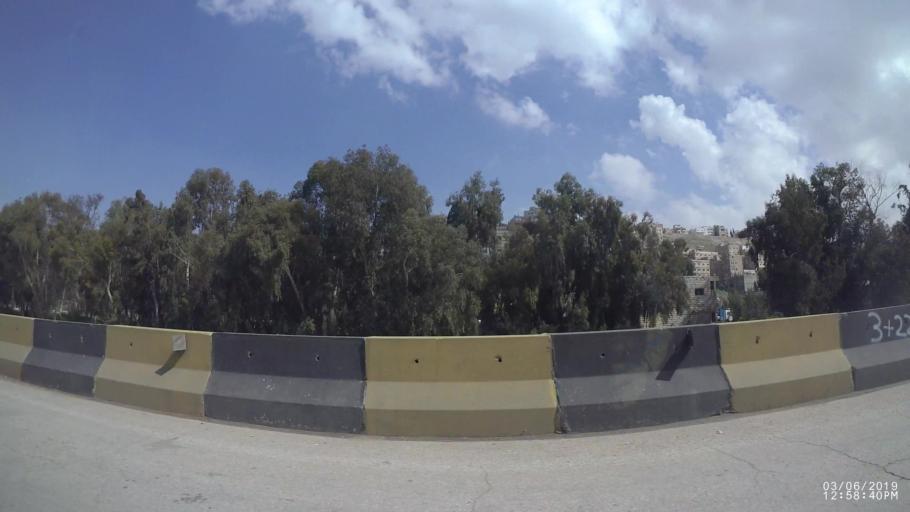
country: JO
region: Amman
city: Amman
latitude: 31.9843
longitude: 35.9762
